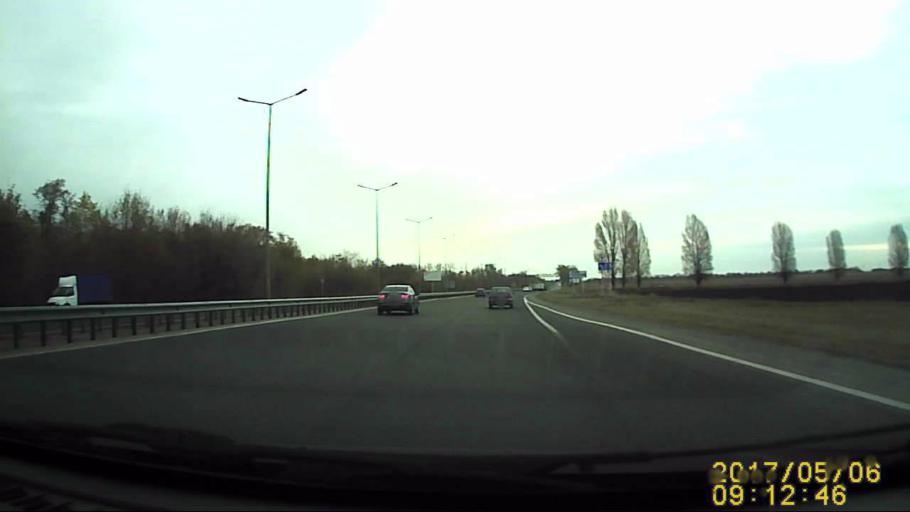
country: RU
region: Ulyanovsk
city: Mirnyy
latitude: 54.3600
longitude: 48.6796
